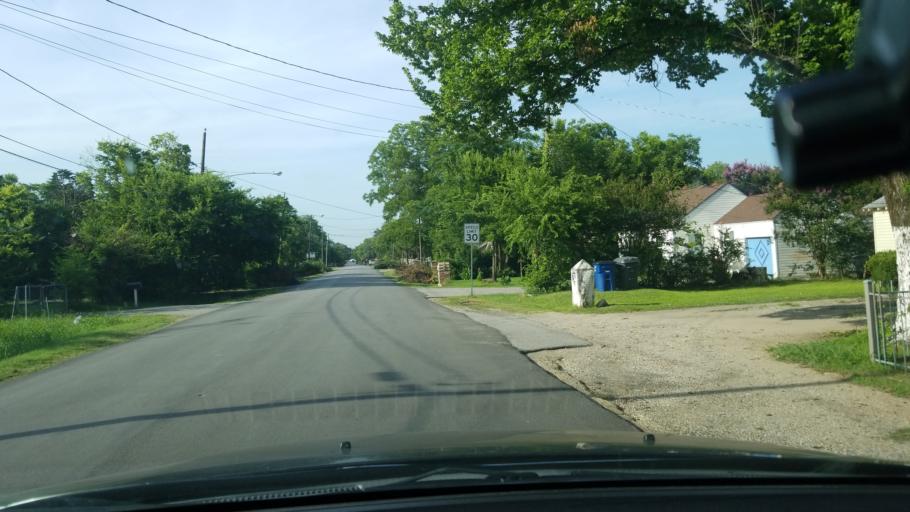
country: US
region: Texas
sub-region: Dallas County
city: Balch Springs
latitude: 32.7285
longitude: -96.6885
